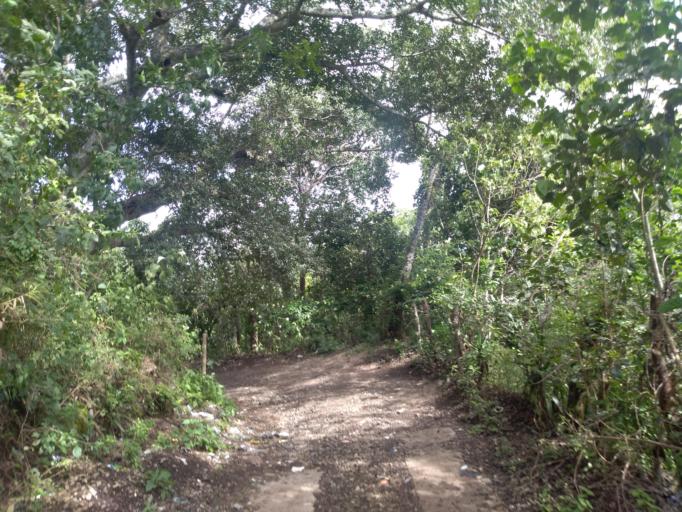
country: GT
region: Escuintla
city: San Vicente Pacaya
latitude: 14.3714
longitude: -90.5690
